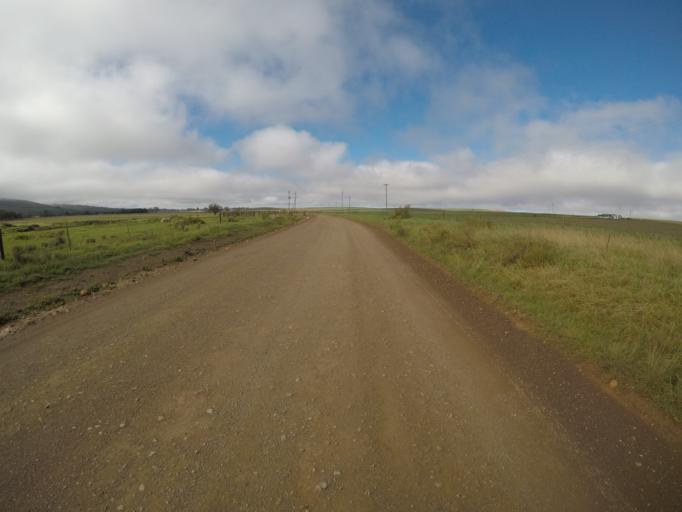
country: ZA
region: Western Cape
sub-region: Cape Winelands District Municipality
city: Ashton
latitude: -34.1481
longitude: 19.8719
